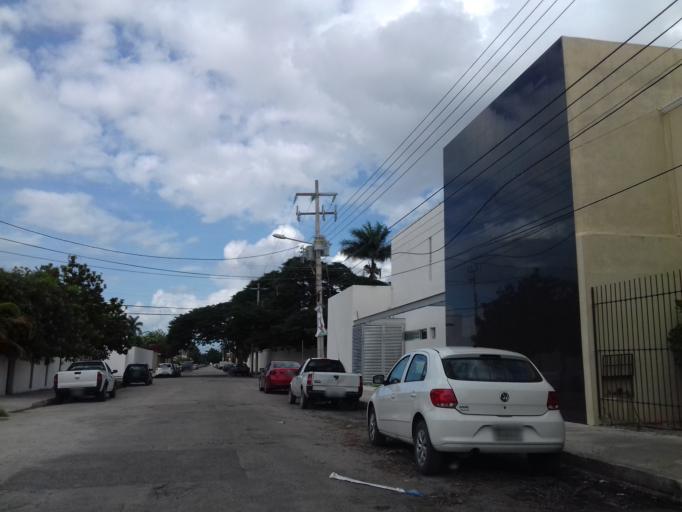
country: MX
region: Yucatan
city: Merida
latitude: 20.9989
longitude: -89.6141
